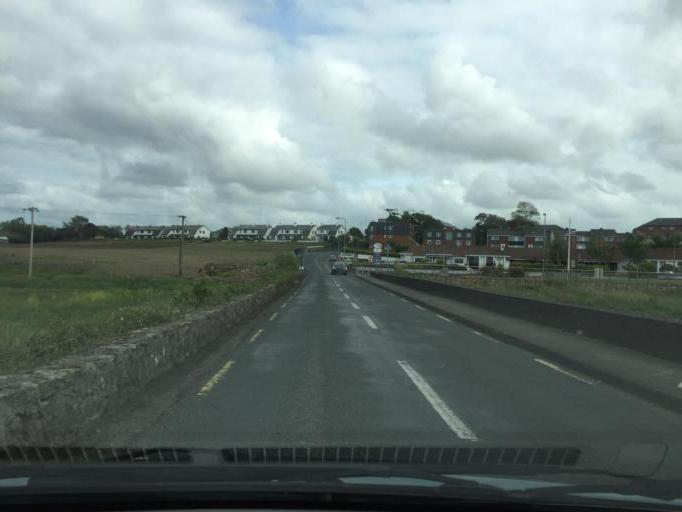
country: IE
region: Connaught
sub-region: Sligo
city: Sligo
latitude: 54.2837
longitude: -8.4770
